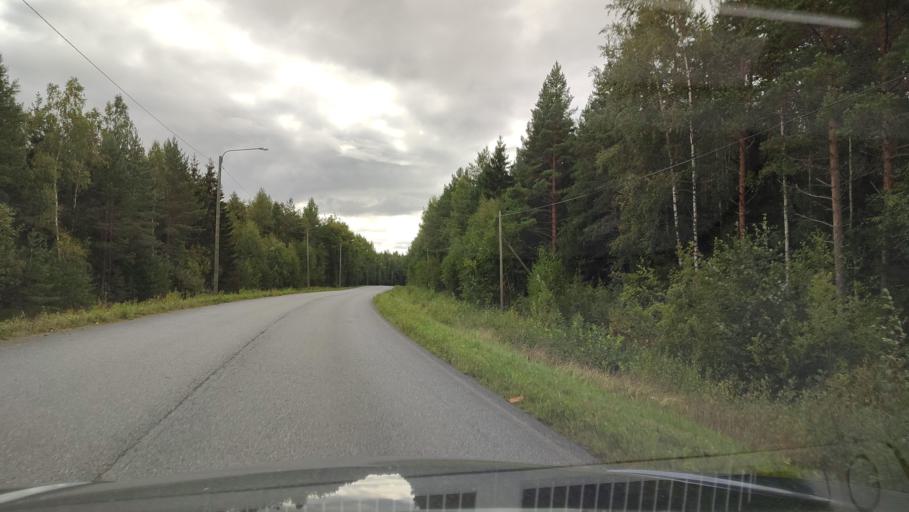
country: FI
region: Ostrobothnia
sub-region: Sydosterbotten
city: Kristinestad
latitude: 62.2622
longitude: 21.3490
